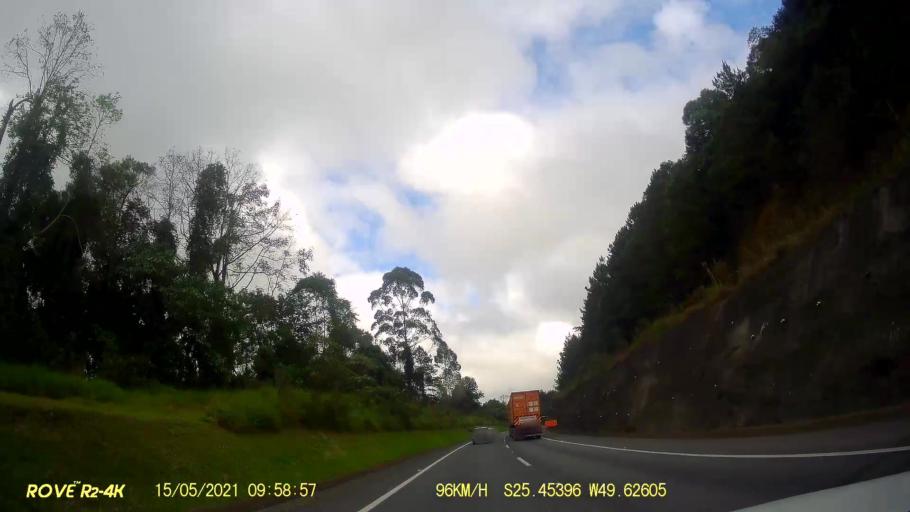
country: BR
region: Parana
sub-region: Campo Largo
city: Campo Largo
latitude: -25.4541
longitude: -49.6261
